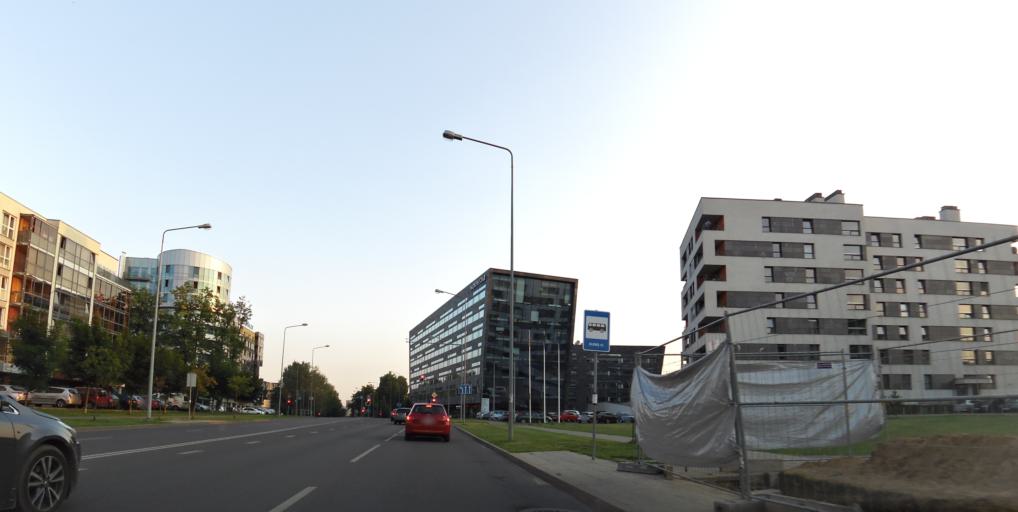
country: LT
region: Vilnius County
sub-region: Vilnius
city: Vilnius
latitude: 54.7093
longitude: 25.2911
